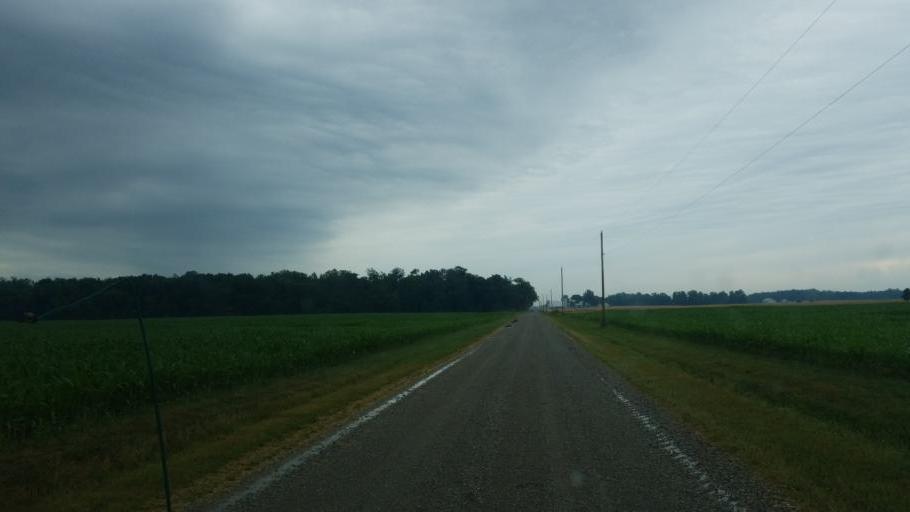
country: US
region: Indiana
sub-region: DeKalb County
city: Butler
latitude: 41.4588
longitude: -84.9100
